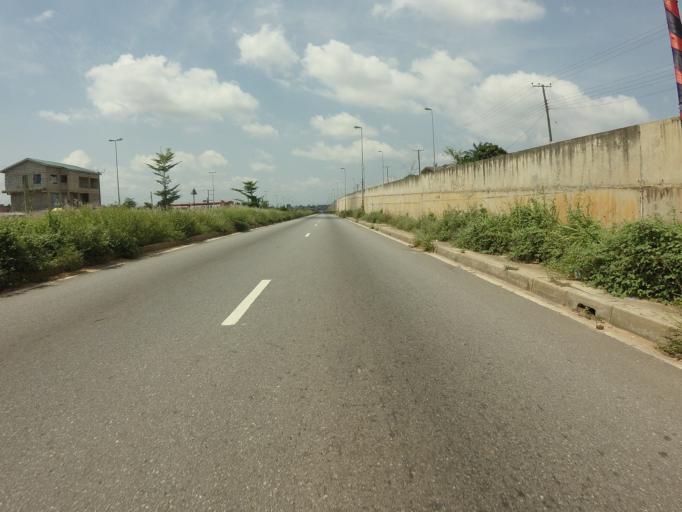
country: GH
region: Greater Accra
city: Gbawe
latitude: 5.6238
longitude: -0.3030
